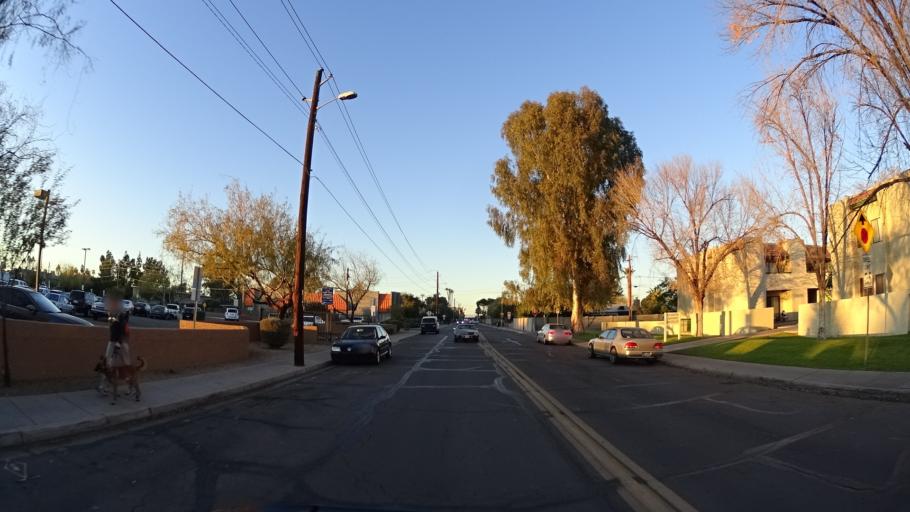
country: US
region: Arizona
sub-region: Maricopa County
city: Tempe
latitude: 33.4161
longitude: -111.9177
